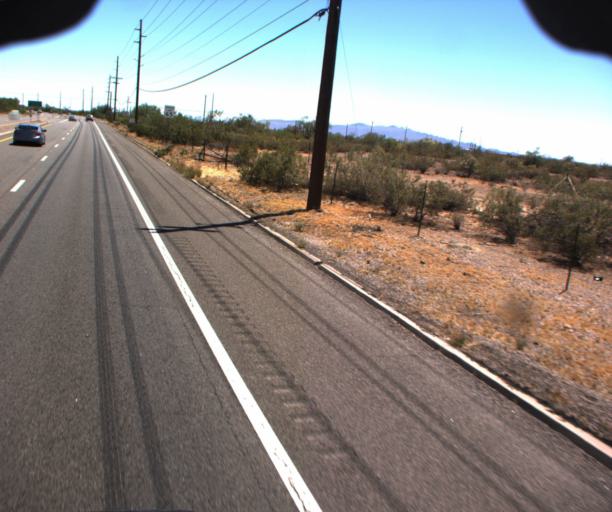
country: US
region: Arizona
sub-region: Maricopa County
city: Wickenburg
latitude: 33.8560
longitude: -112.6248
